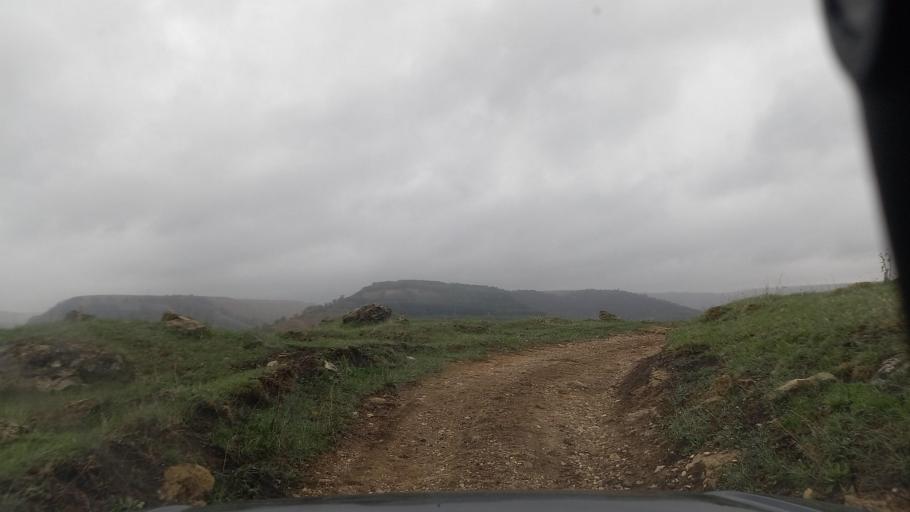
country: RU
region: Stavropol'skiy
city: Nezhinskiy
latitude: 43.8495
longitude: 42.6362
